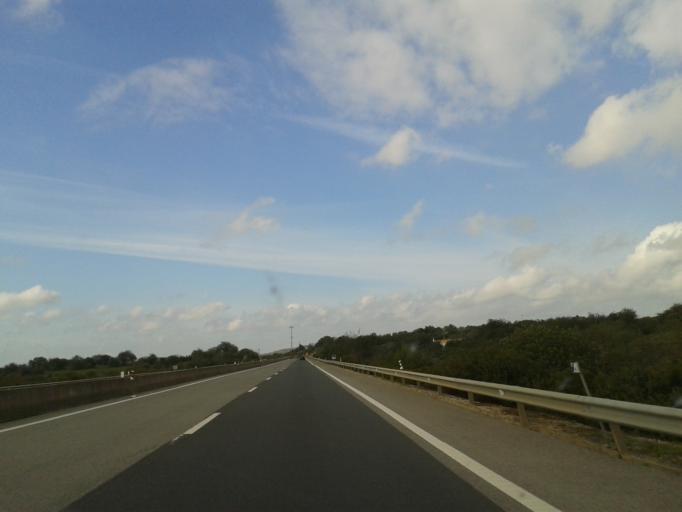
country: PT
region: Faro
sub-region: Tavira
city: Luz
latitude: 37.1355
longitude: -7.7263
